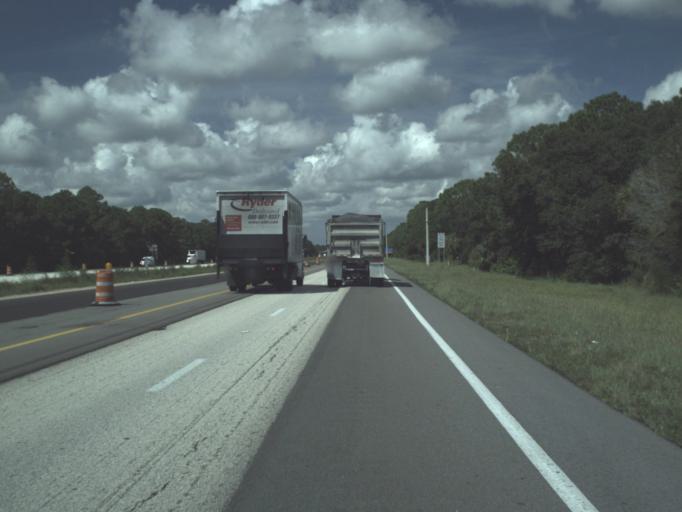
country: US
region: Florida
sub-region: Sarasota County
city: North Port
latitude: 27.0991
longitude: -82.1664
